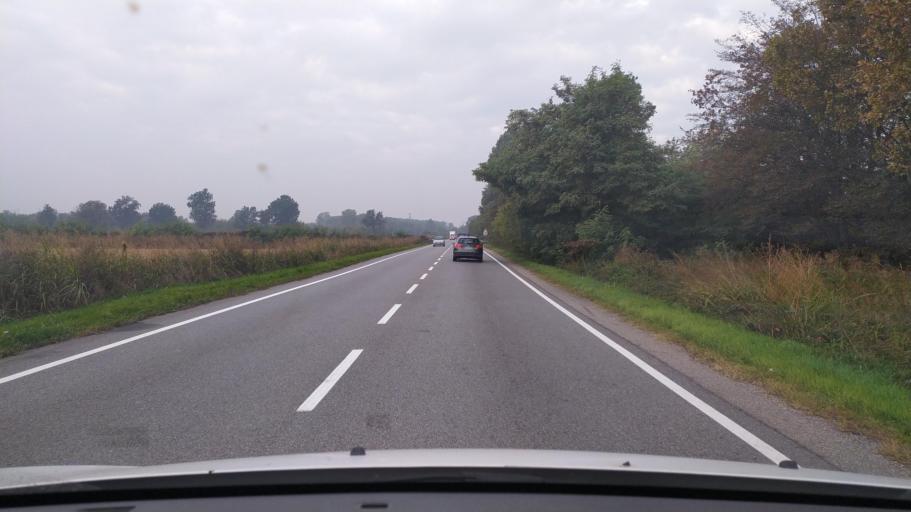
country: IT
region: Lombardy
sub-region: Citta metropolitana di Milano
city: Cusago
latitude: 45.4444
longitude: 9.0154
